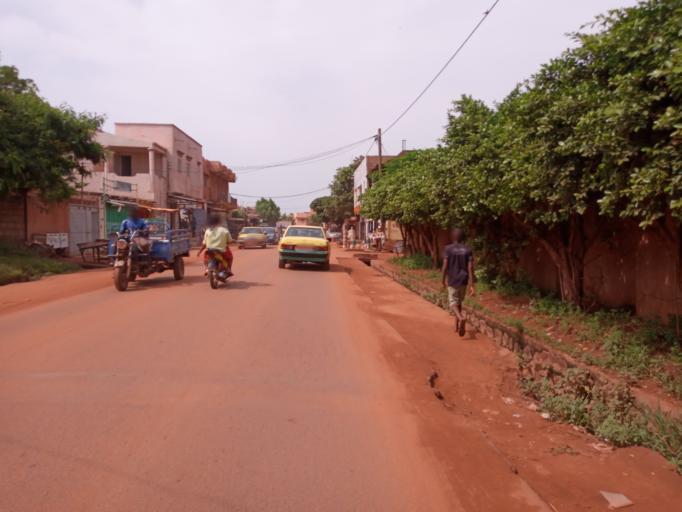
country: ML
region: Bamako
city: Bamako
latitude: 12.5627
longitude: -7.9902
